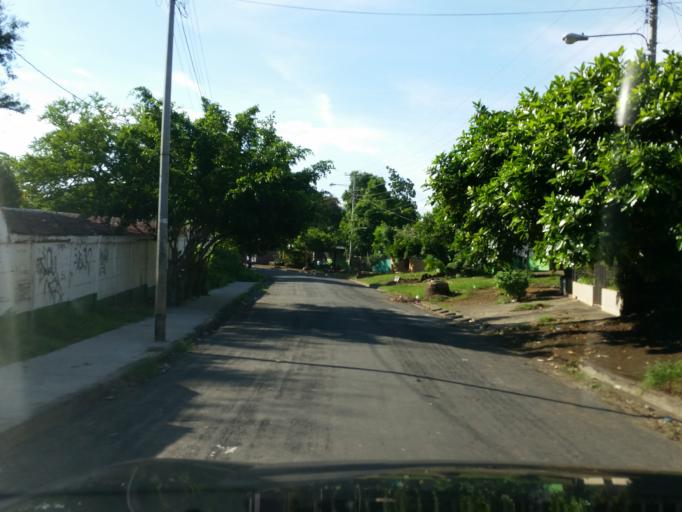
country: NI
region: Managua
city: Managua
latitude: 12.1101
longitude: -86.2247
